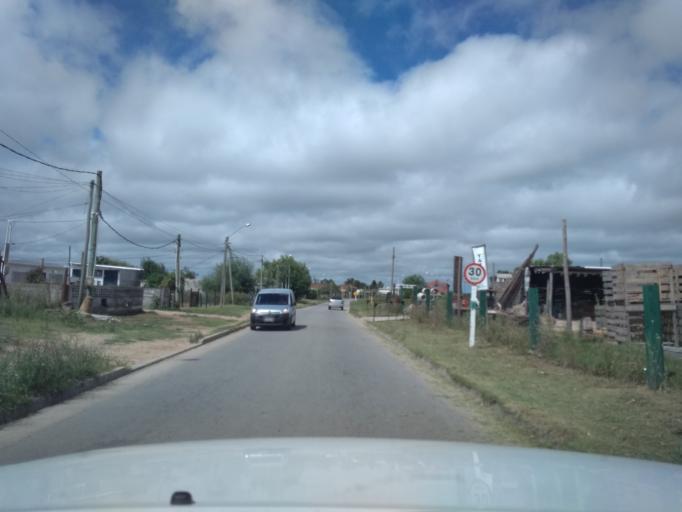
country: UY
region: Canelones
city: Pando
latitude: -34.7167
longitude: -55.9660
